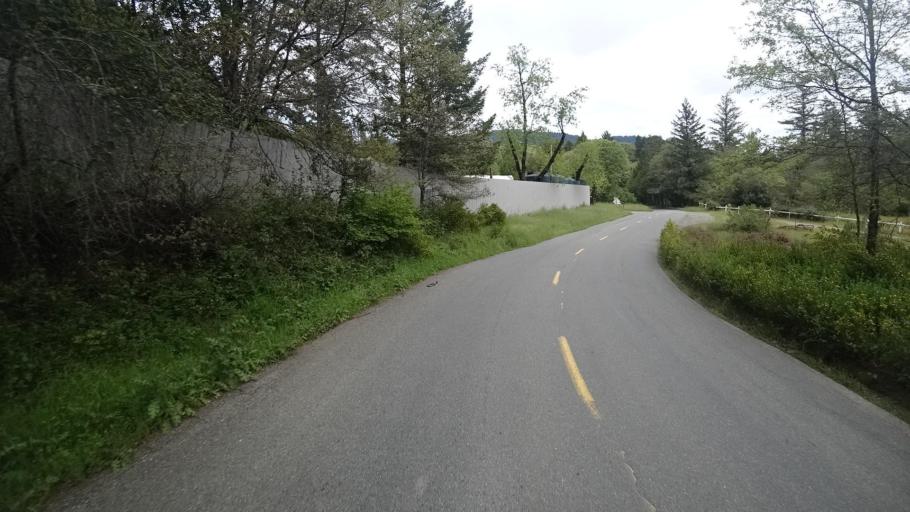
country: US
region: California
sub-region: Humboldt County
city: Redway
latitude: 40.1026
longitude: -123.9074
